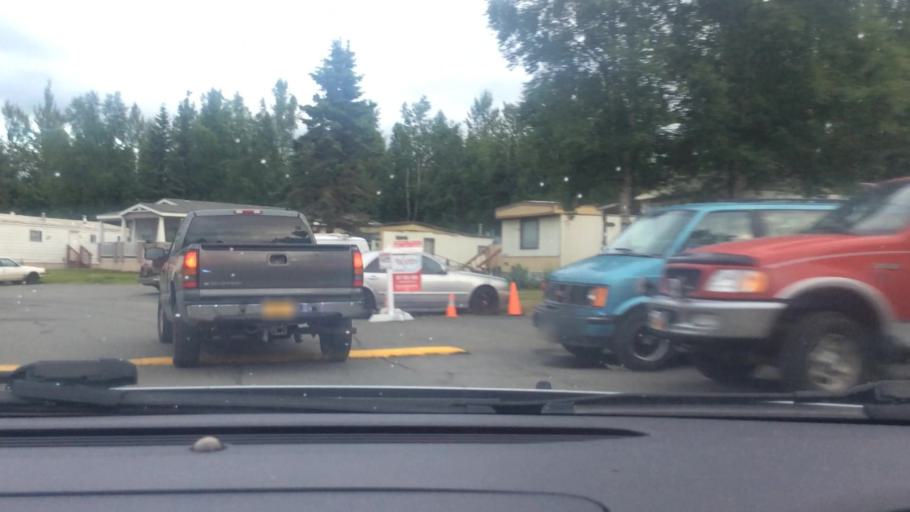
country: US
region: Alaska
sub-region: Anchorage Municipality
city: Elmendorf Air Force Base
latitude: 61.1986
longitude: -149.7276
